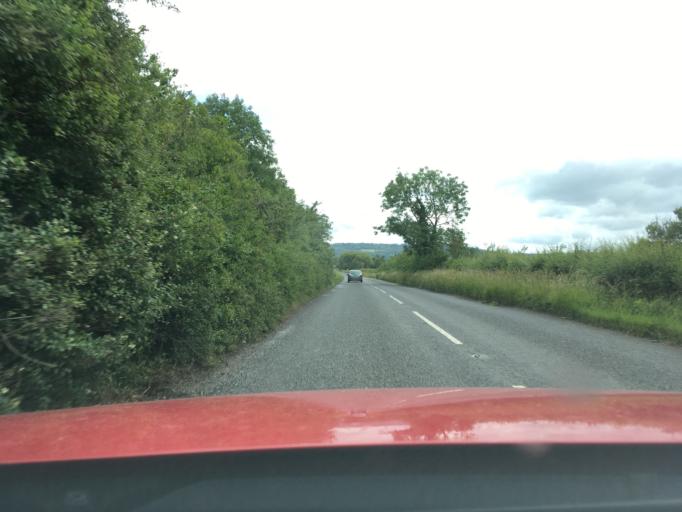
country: GB
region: England
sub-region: Gloucestershire
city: Winchcombe
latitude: 51.9953
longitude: -1.9679
